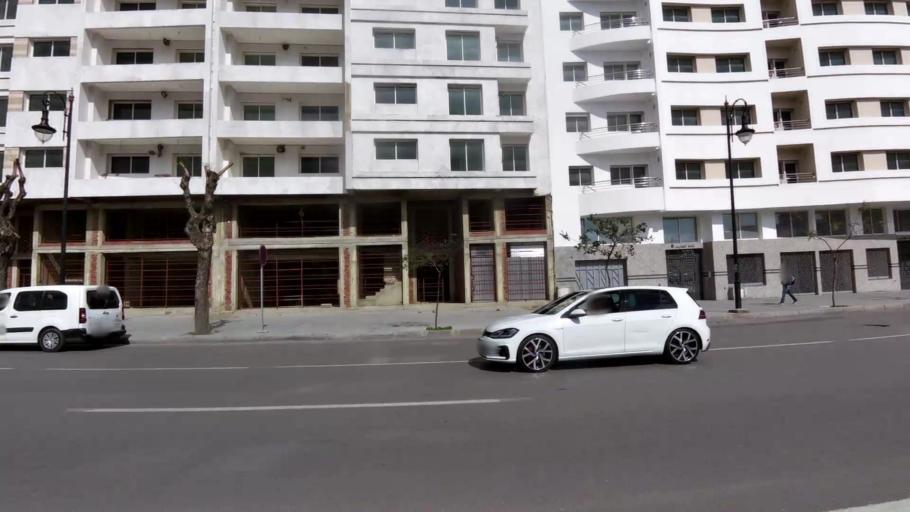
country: MA
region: Tanger-Tetouan
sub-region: Tanger-Assilah
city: Tangier
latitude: 35.7650
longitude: -5.8134
